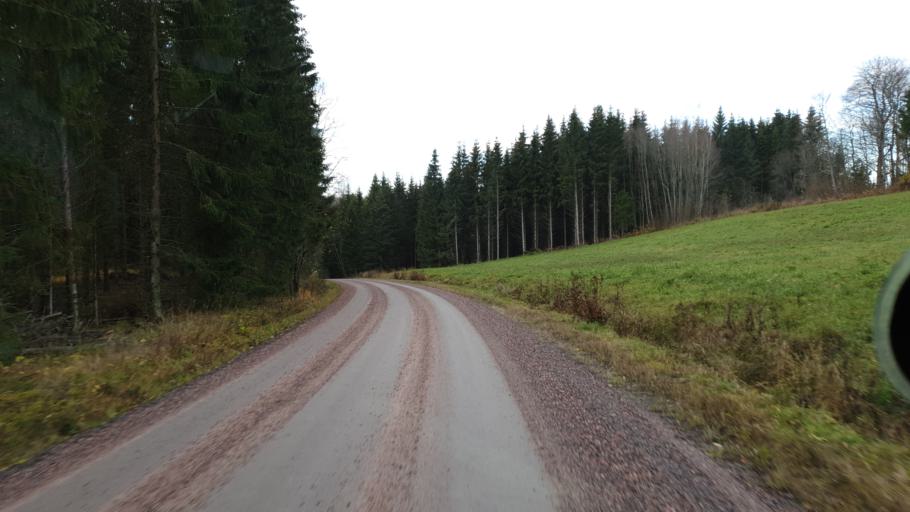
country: FI
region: Uusimaa
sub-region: Helsinki
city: Siuntio
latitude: 60.1481
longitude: 24.2726
